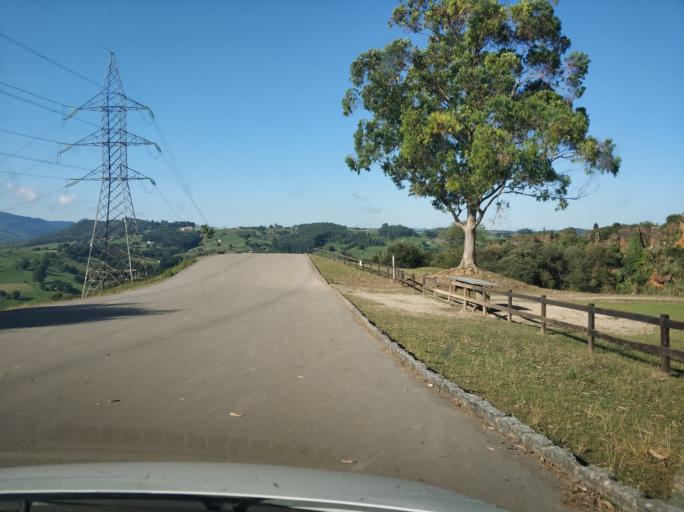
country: ES
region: Cantabria
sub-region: Provincia de Cantabria
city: Penagos
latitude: 43.3452
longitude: -3.8489
